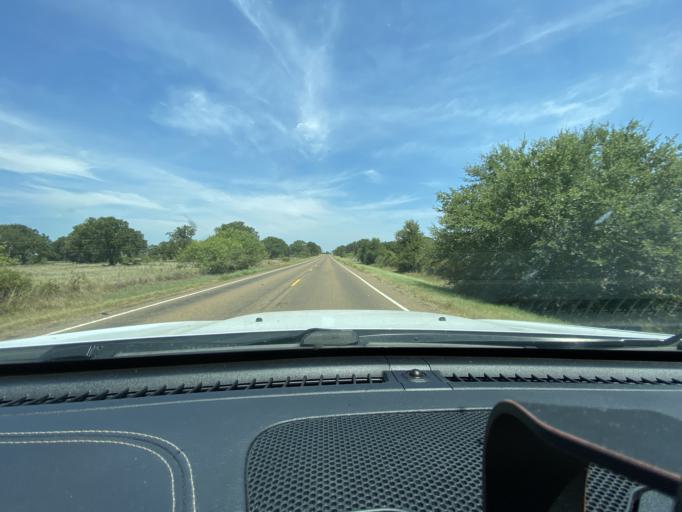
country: US
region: Texas
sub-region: Bastrop County
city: Smithville
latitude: 30.1081
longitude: -97.0792
